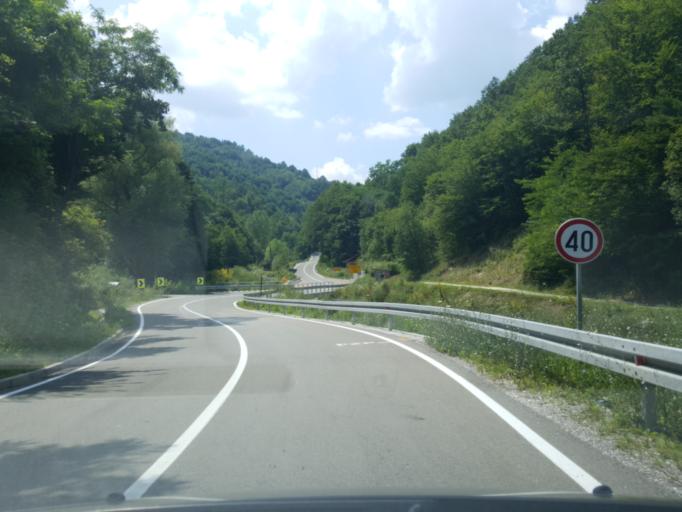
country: RS
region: Central Serbia
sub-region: Sumadijski Okrug
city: Arangelovac
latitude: 44.1671
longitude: 20.5146
